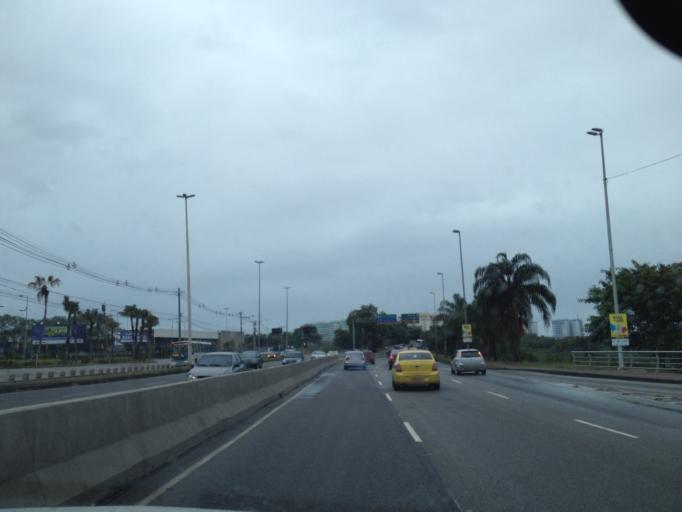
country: BR
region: Rio de Janeiro
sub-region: Sao Joao De Meriti
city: Sao Joao de Meriti
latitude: -22.9637
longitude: -43.3572
